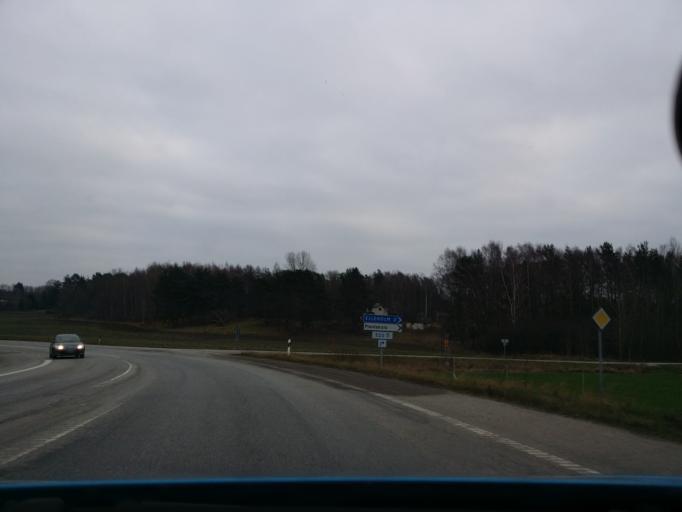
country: SE
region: Blekinge
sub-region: Karlshamns Kommun
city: Morrum
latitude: 56.1756
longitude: 14.7286
